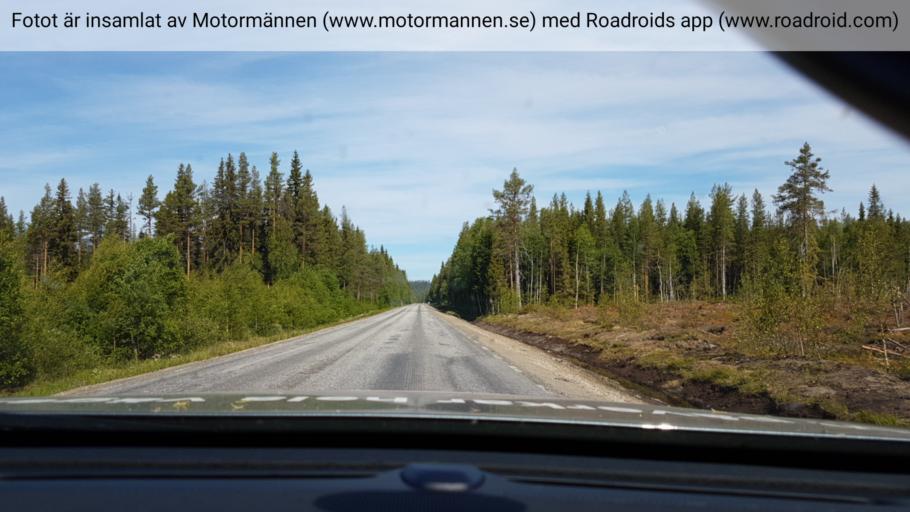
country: SE
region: Vaesterbotten
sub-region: Dorotea Kommun
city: Dorotea
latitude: 64.3164
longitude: 16.3240
